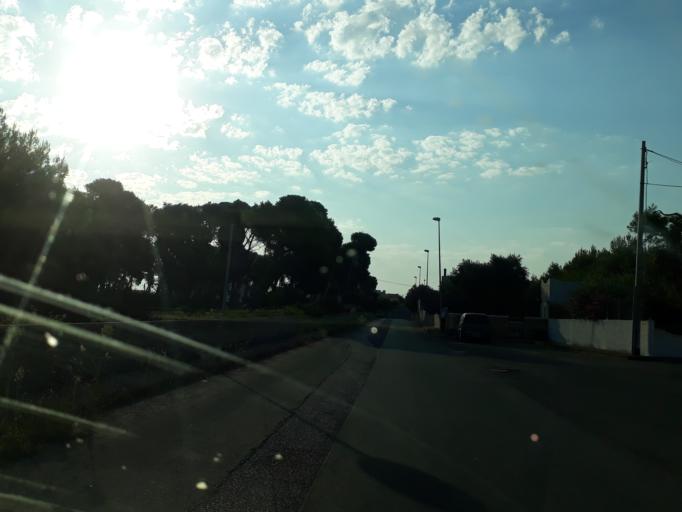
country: IT
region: Apulia
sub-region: Provincia di Brindisi
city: Carovigno
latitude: 40.7545
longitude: 17.7047
